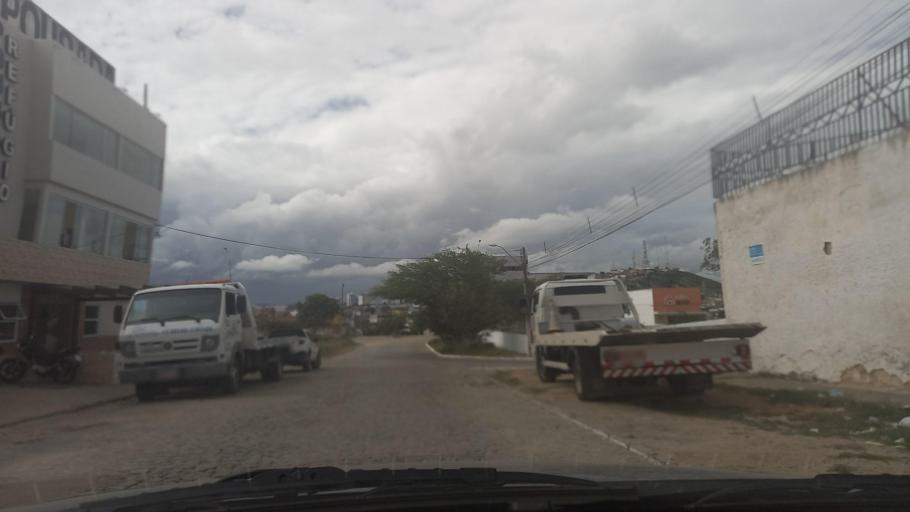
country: BR
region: Pernambuco
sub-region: Caruaru
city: Caruaru
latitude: -8.2936
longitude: -35.9887
